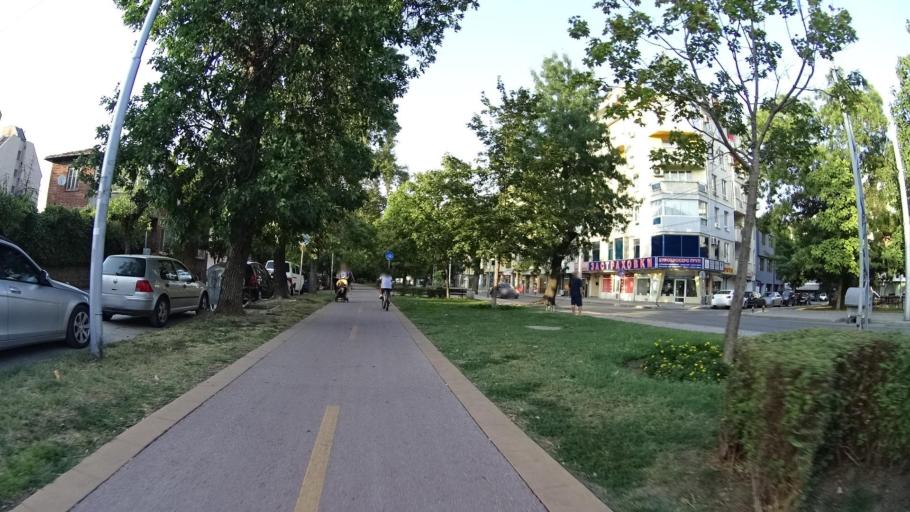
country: BG
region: Plovdiv
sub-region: Obshtina Plovdiv
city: Plovdiv
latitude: 42.1285
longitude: 24.7430
